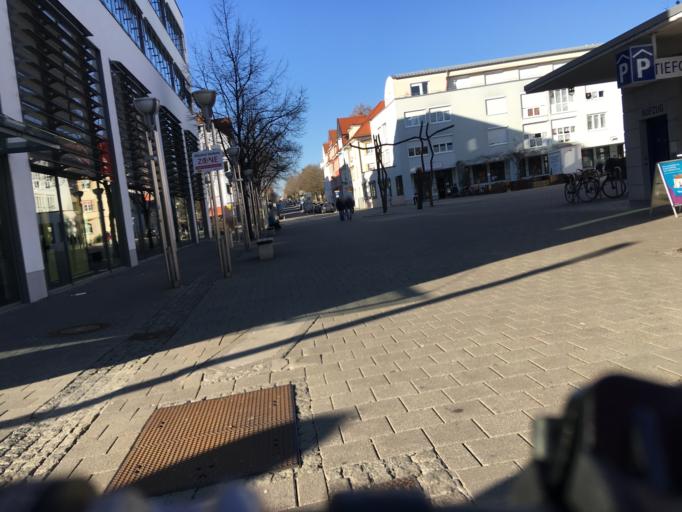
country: DE
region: Baden-Wuerttemberg
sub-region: Freiburg Region
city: Singen
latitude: 47.7628
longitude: 8.8380
